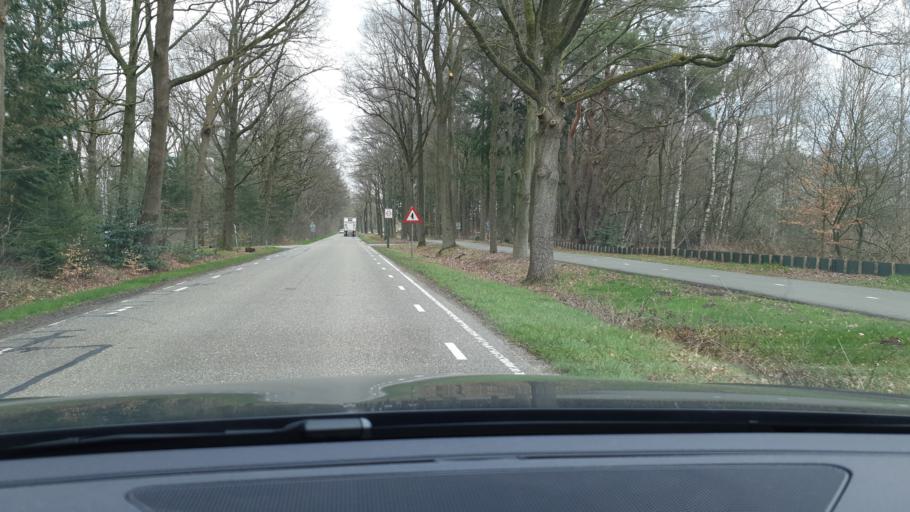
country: NL
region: North Brabant
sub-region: Gemeente Oirschot
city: Oostelbeers
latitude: 51.4327
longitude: 5.3132
